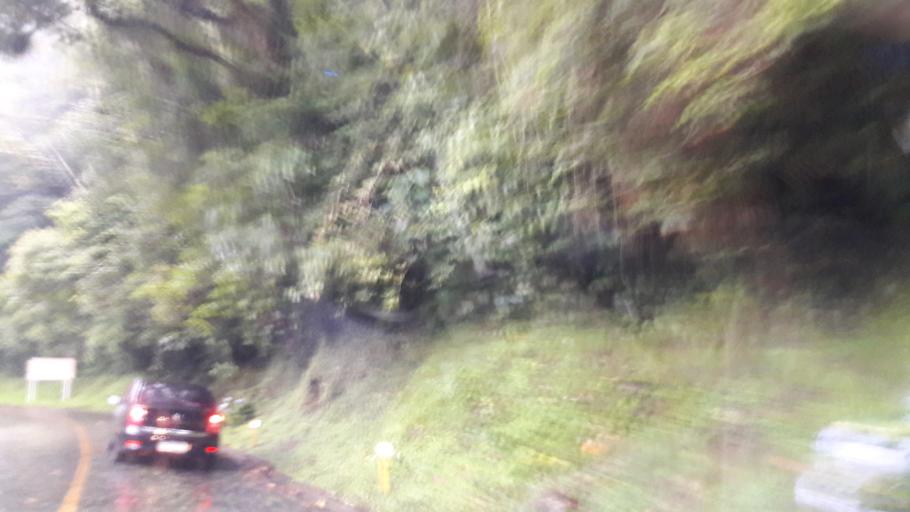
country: BR
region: Parana
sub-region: Campina Grande Do Sul
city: Campina Grande do Sul
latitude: -25.3484
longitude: -48.8863
